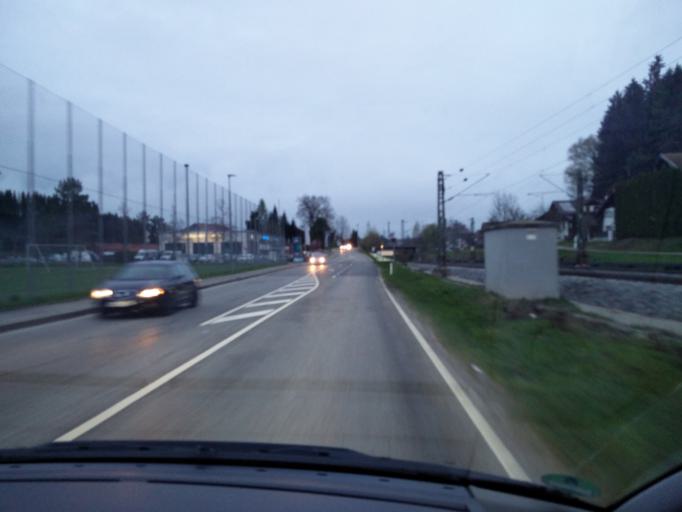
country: DE
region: Bavaria
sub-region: Upper Bavaria
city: Bad Endorf
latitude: 47.8996
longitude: 12.3052
